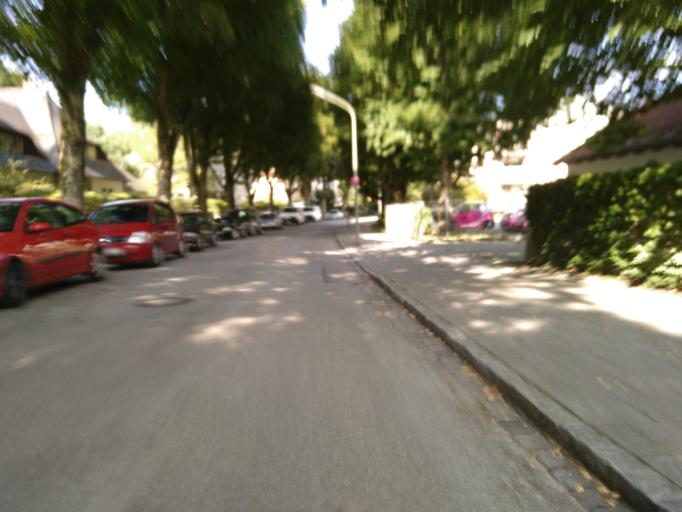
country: DE
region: Bavaria
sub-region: Upper Bavaria
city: Munich
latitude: 48.1029
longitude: 11.5803
